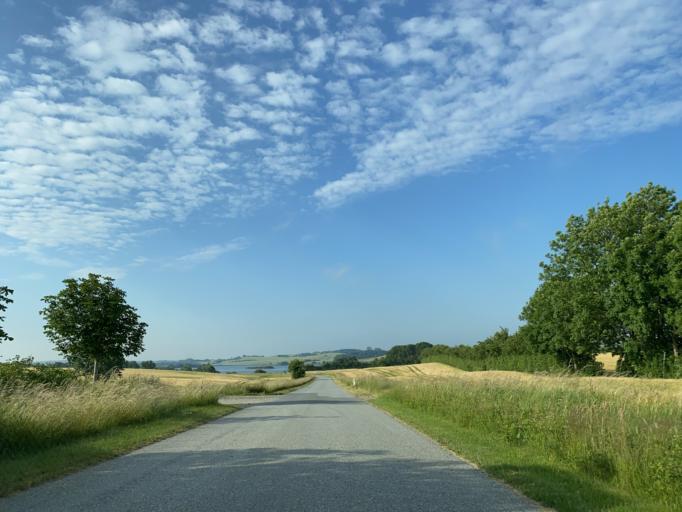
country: DK
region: South Denmark
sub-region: Haderslev Kommune
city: Haderslev
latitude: 55.1774
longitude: 9.4814
